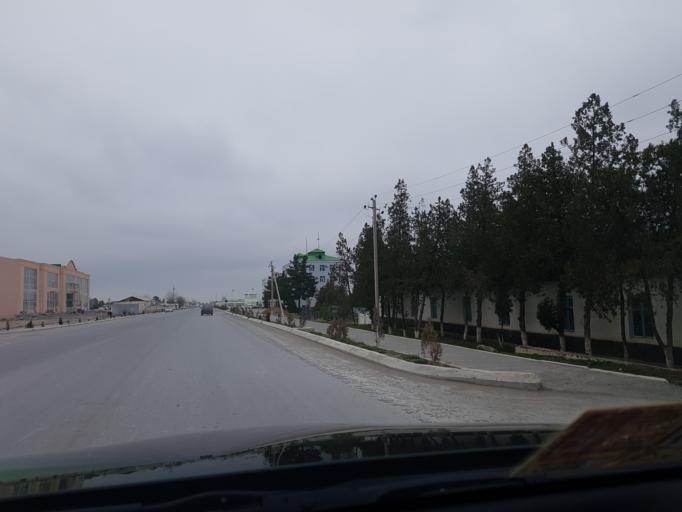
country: TM
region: Ahal
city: Abadan
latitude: 38.1416
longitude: 57.9507
